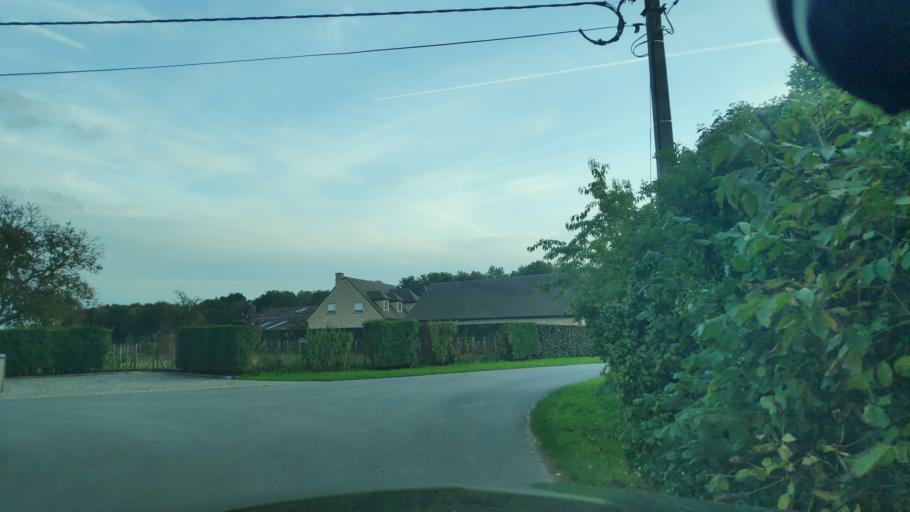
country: BE
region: Flanders
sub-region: Provincie Oost-Vlaanderen
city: Aalter
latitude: 51.1101
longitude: 3.4699
